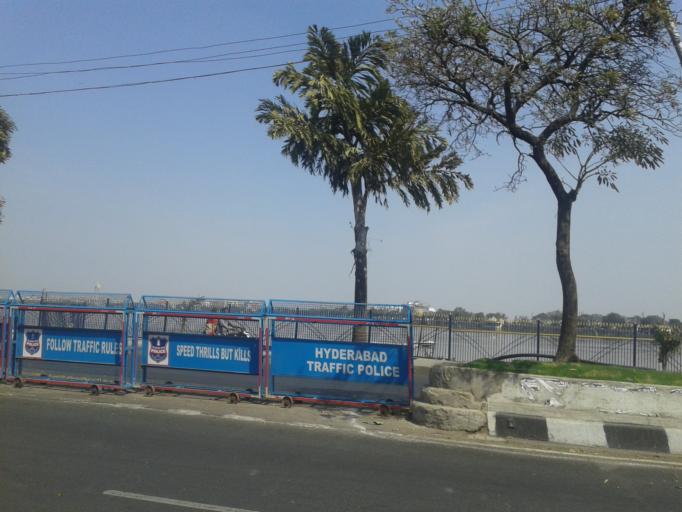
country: IN
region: Telangana
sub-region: Hyderabad
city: Hyderabad
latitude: 17.4112
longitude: 78.4713
